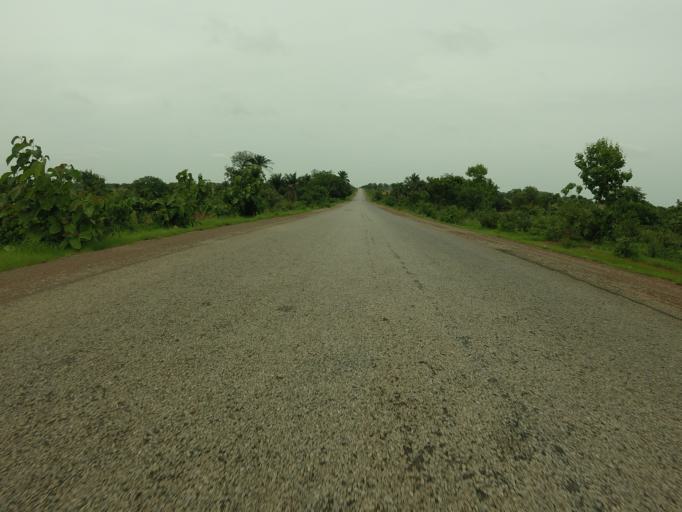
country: GH
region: Northern
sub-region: Yendi
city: Yendi
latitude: 9.4027
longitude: -0.0104
